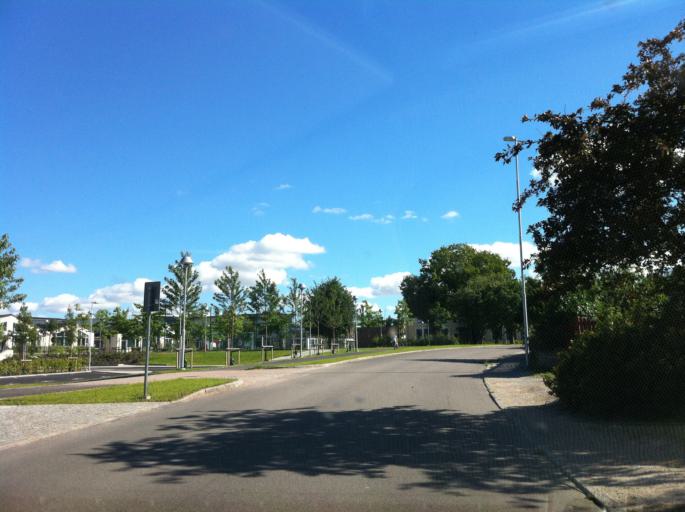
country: SE
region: Skane
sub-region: Svalovs Kommun
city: Kagerod
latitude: 56.0205
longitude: 13.1117
